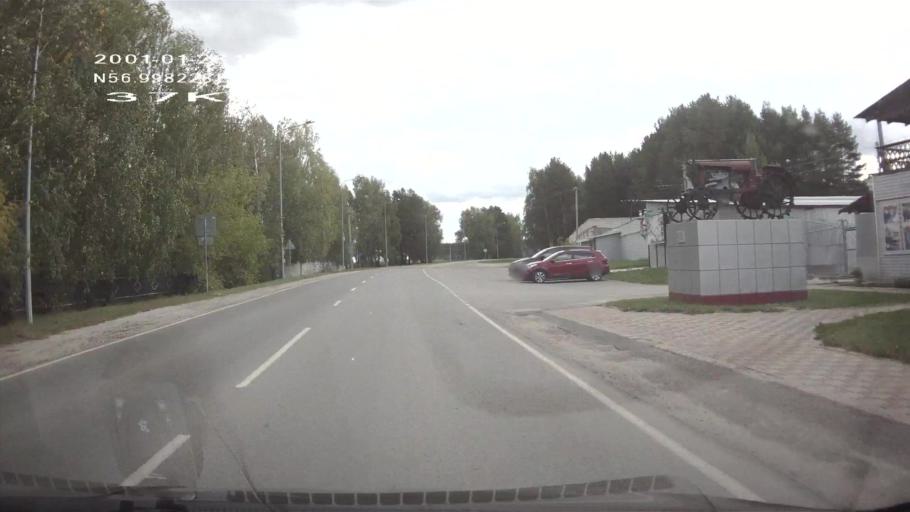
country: RU
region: Mariy-El
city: Kuzhener
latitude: 56.9979
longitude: 48.7412
